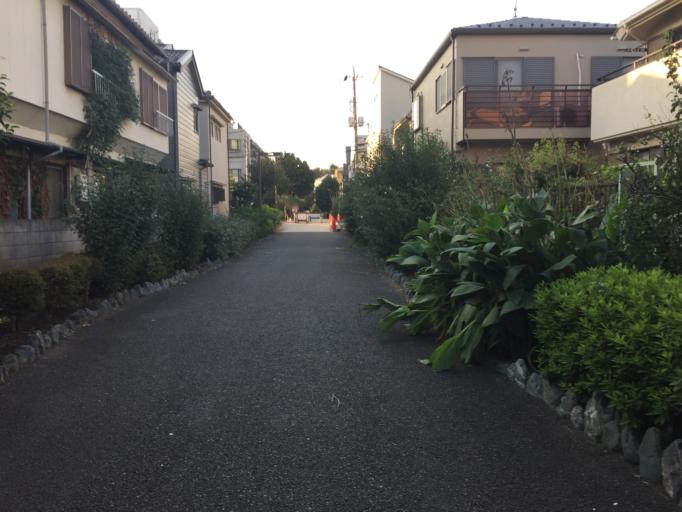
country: JP
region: Tokyo
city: Tokyo
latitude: 35.6466
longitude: 139.6640
